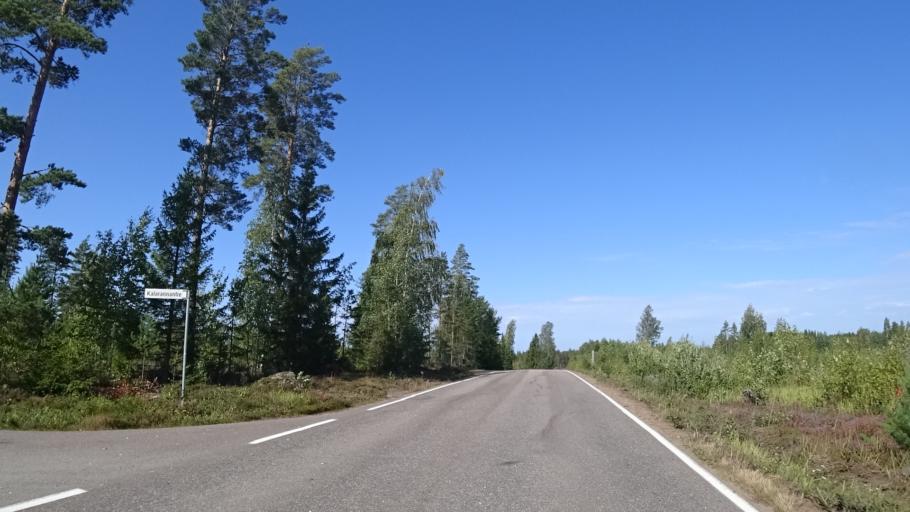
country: FI
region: Kymenlaakso
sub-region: Kotka-Hamina
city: Hamina
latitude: 60.5252
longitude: 27.3103
